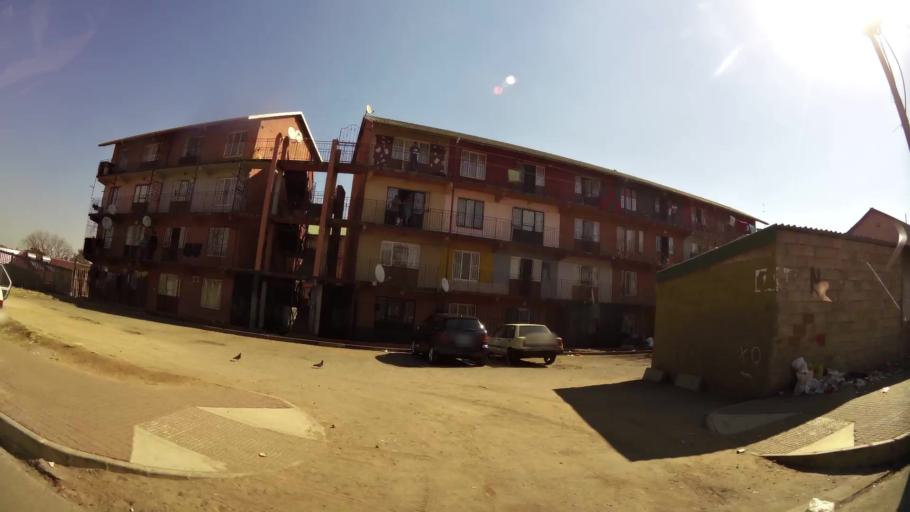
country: ZA
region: Gauteng
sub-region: City of Johannesburg Metropolitan Municipality
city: Johannesburg
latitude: -26.1841
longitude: 27.9682
